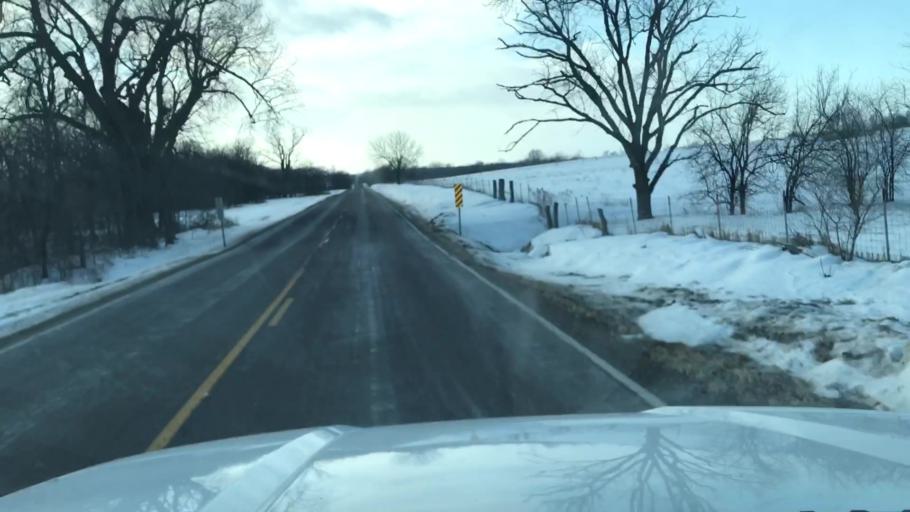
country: US
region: Missouri
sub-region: Nodaway County
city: Maryville
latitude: 40.2018
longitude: -94.9358
